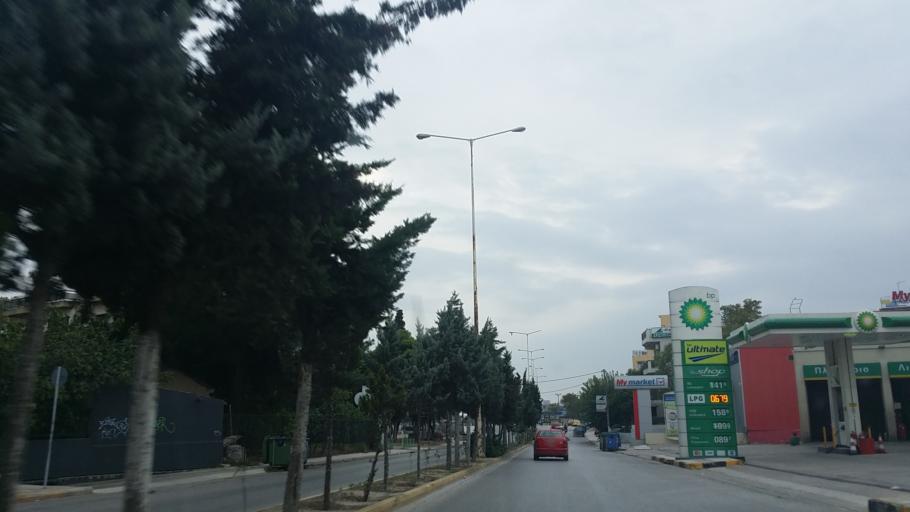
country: GR
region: Attica
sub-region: Nomarchia Athinas
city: Metamorfosi
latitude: 38.0619
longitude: 23.7570
